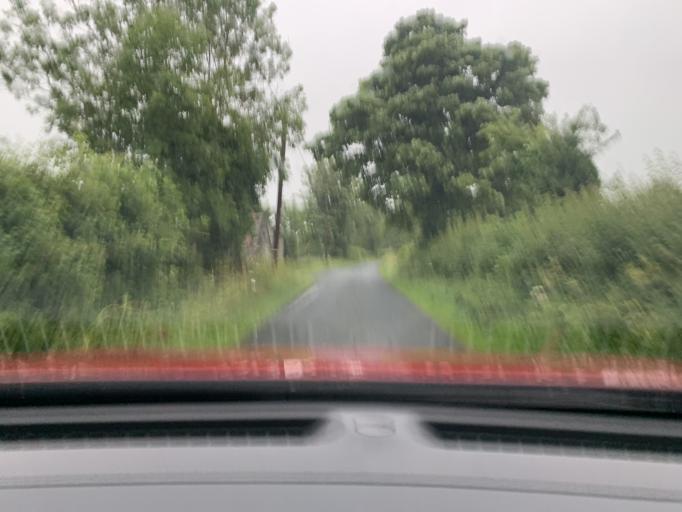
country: IE
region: Connaught
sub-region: Sligo
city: Sligo
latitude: 54.3192
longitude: -8.4622
